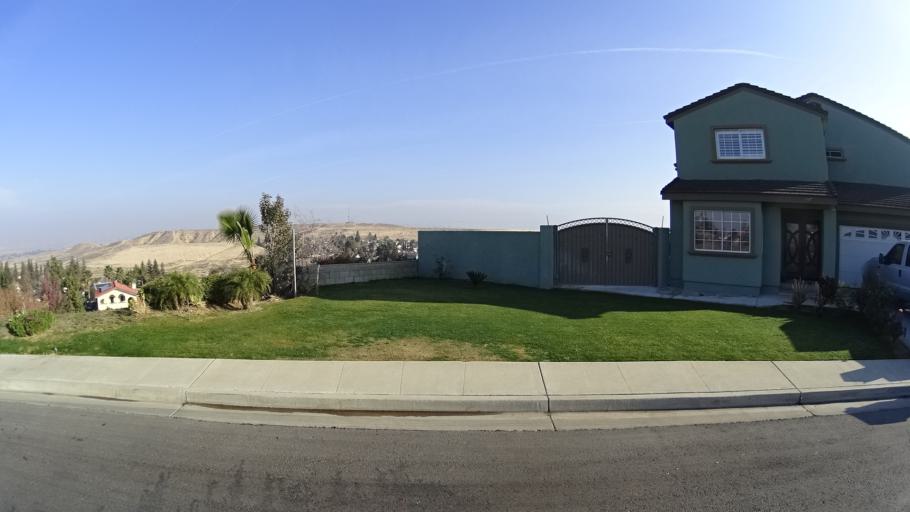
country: US
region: California
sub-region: Kern County
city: Oildale
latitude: 35.4070
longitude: -118.9344
